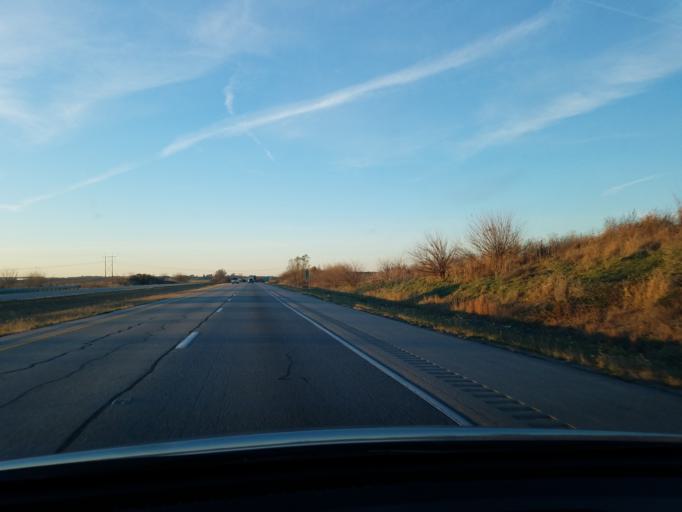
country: US
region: Indiana
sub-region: Posey County
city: Poseyville
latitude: 38.1734
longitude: -87.7553
